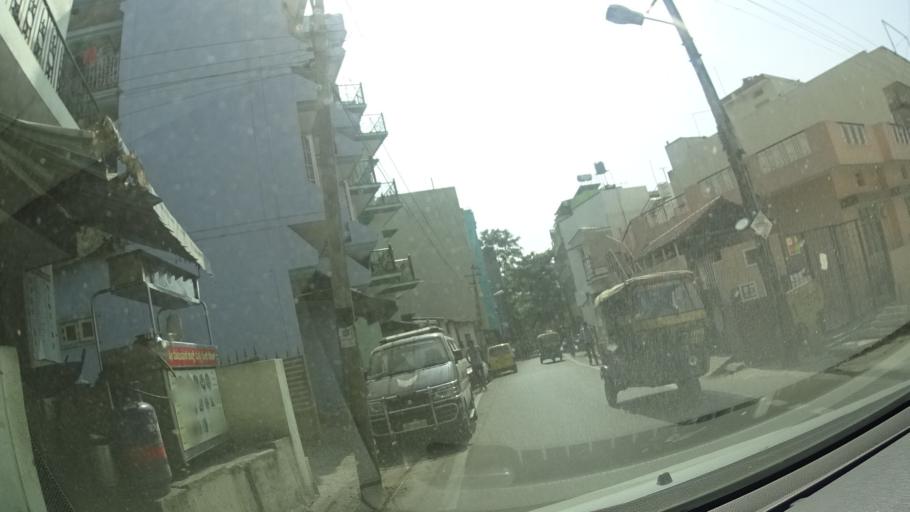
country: IN
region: Karnataka
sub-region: Bangalore Urban
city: Bangalore
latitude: 12.9552
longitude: 77.5567
